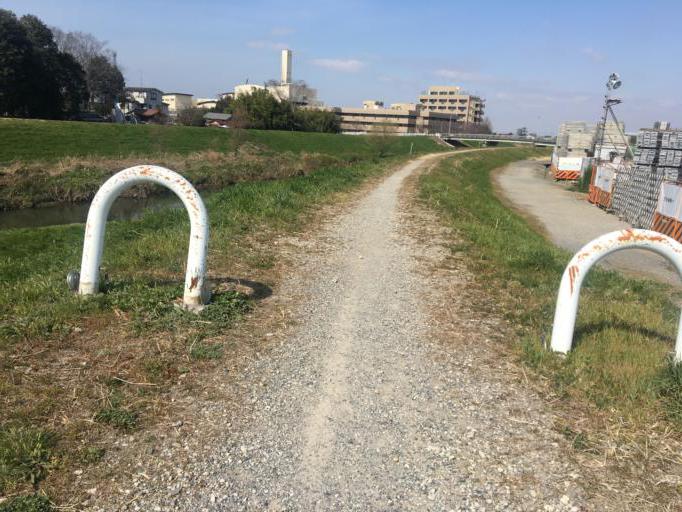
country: JP
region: Saitama
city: Oi
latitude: 35.8679
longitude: 139.5502
